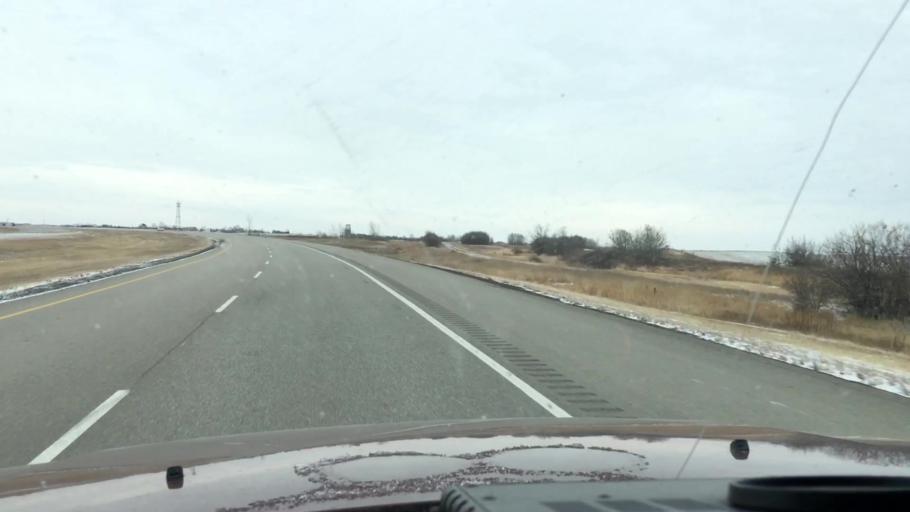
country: CA
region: Saskatchewan
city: Watrous
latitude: 51.3807
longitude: -106.1596
